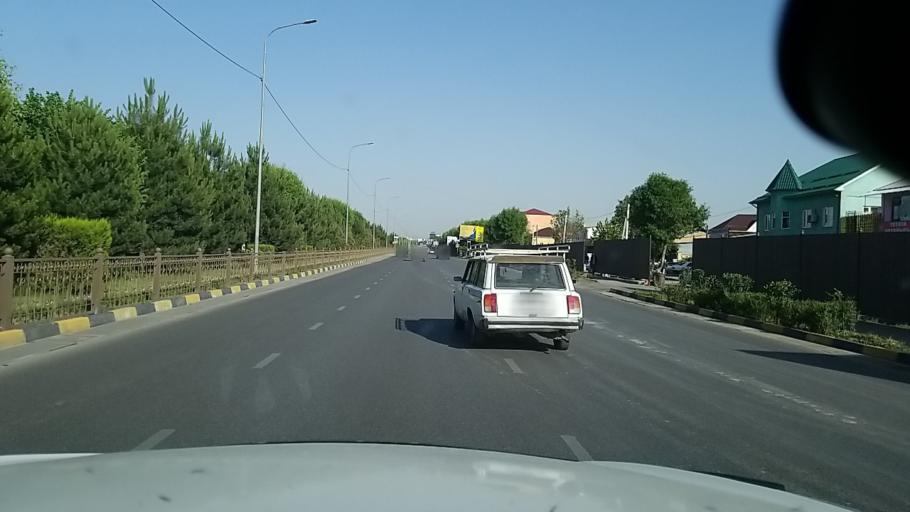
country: KZ
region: Ongtustik Qazaqstan
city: Shymkent
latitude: 42.3335
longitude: 69.5590
